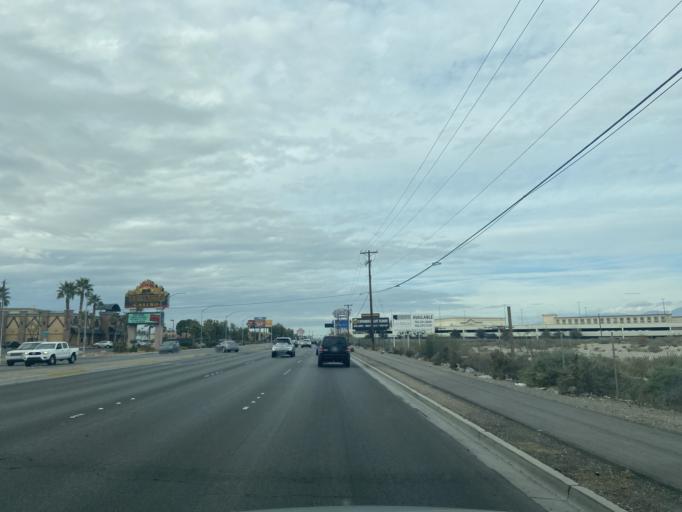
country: US
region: Nevada
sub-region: Clark County
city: Las Vegas
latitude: 36.1933
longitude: -115.1902
